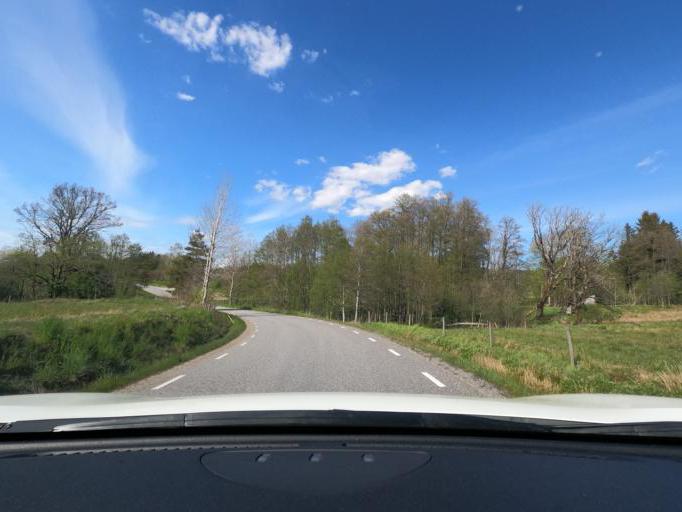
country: SE
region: Vaestra Goetaland
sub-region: Harryda Kommun
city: Ravlanda
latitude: 57.6283
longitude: 12.5006
